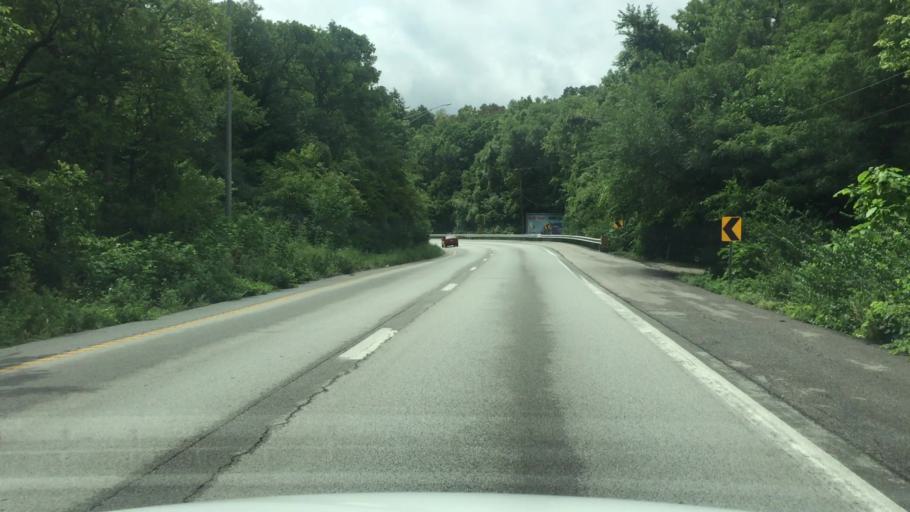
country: US
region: Missouri
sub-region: Jackson County
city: Lees Summit
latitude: 38.9553
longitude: -94.4214
